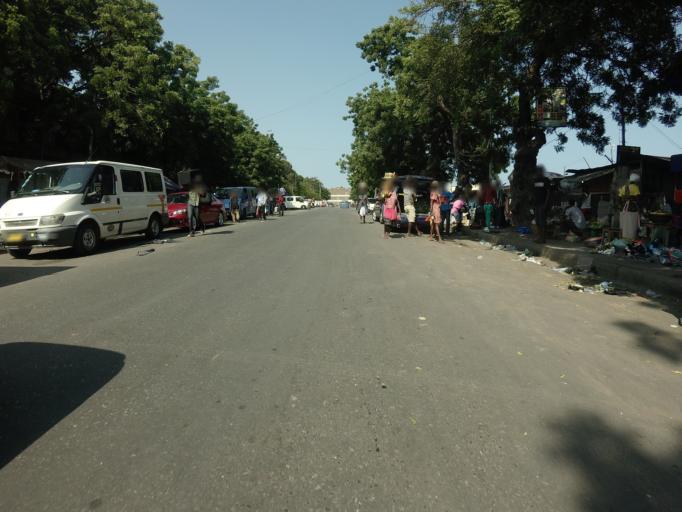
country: GH
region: Greater Accra
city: Accra
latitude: 5.5505
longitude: -0.2063
